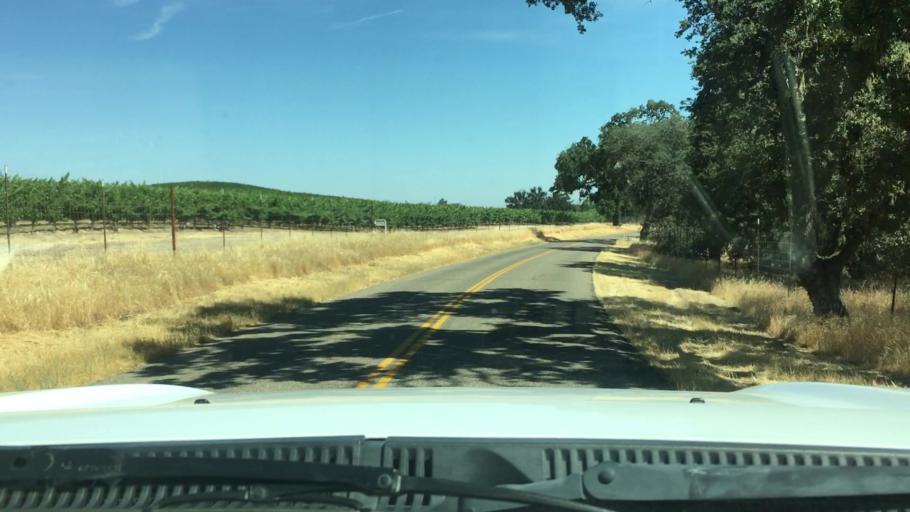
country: US
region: California
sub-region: San Luis Obispo County
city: Templeton
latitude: 35.5672
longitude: -120.6073
